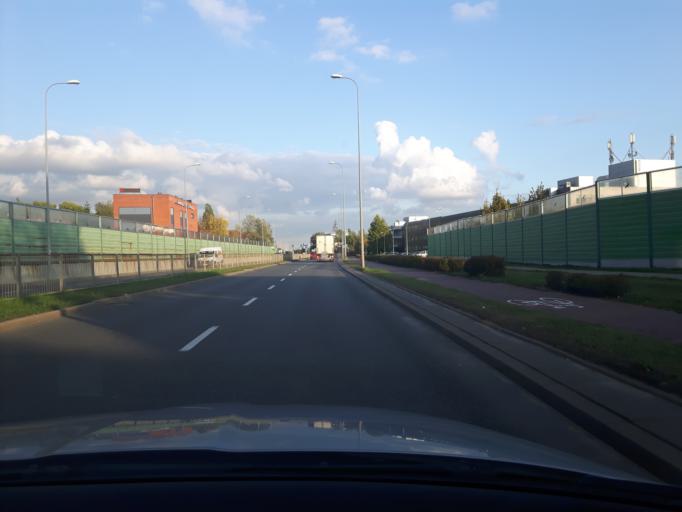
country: PL
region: Masovian Voivodeship
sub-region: Warszawa
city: Ursynow
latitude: 52.1556
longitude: 21.0031
